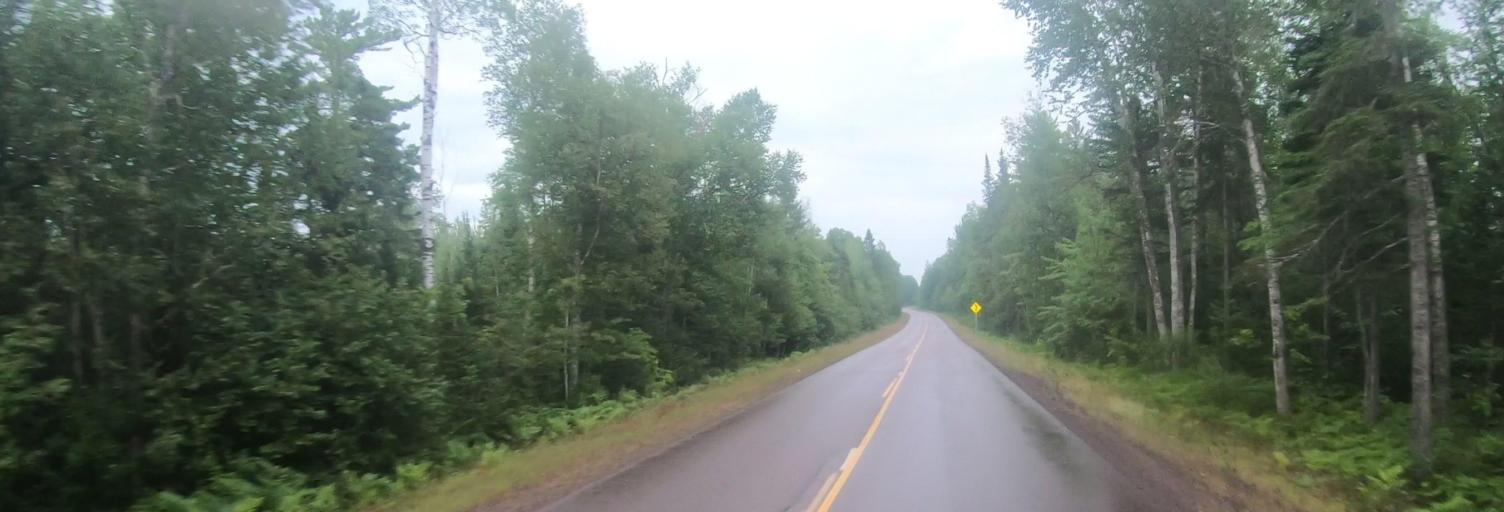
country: US
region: Michigan
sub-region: Keweenaw County
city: Eagle River
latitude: 47.2831
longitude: -88.2780
